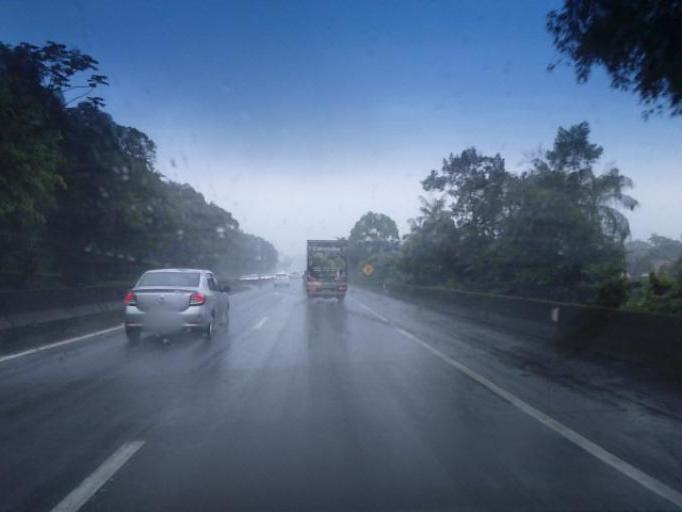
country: BR
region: Santa Catarina
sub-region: Joinville
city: Joinville
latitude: -26.2089
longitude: -48.9152
